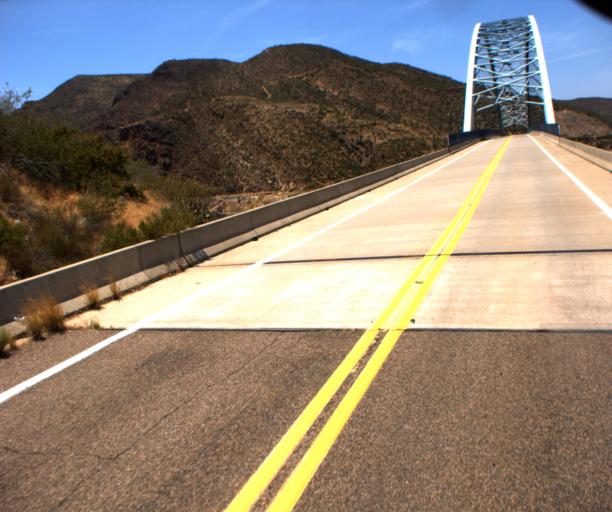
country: US
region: Arizona
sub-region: Gila County
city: Tonto Basin
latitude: 33.6728
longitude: -111.1550
